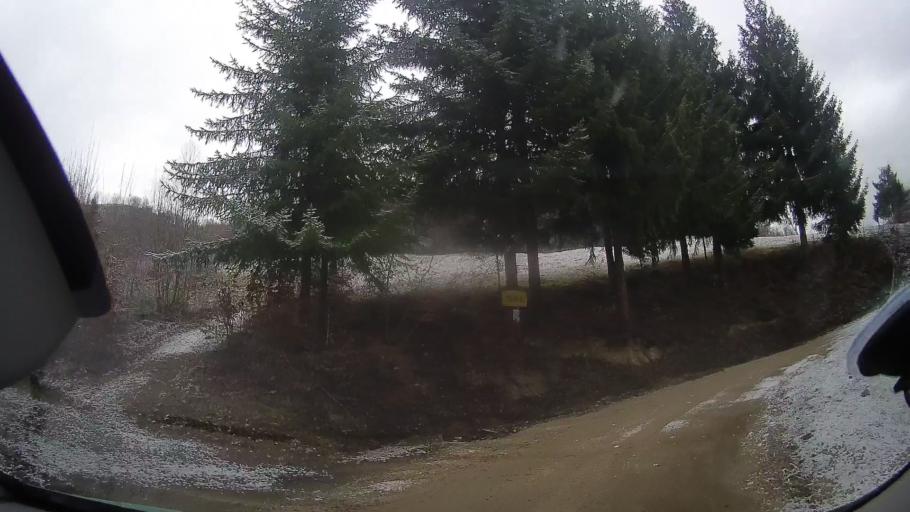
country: RO
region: Cluj
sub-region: Comuna Maguri-Racatau
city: Maguri-Racatau
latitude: 46.6557
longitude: 23.1879
